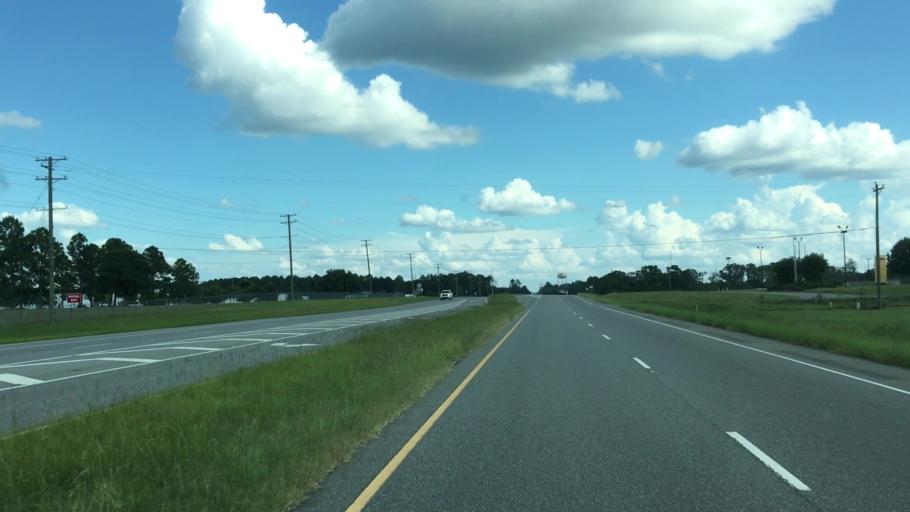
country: US
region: Georgia
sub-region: Laurens County
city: Dublin
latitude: 32.5094
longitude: -82.9493
